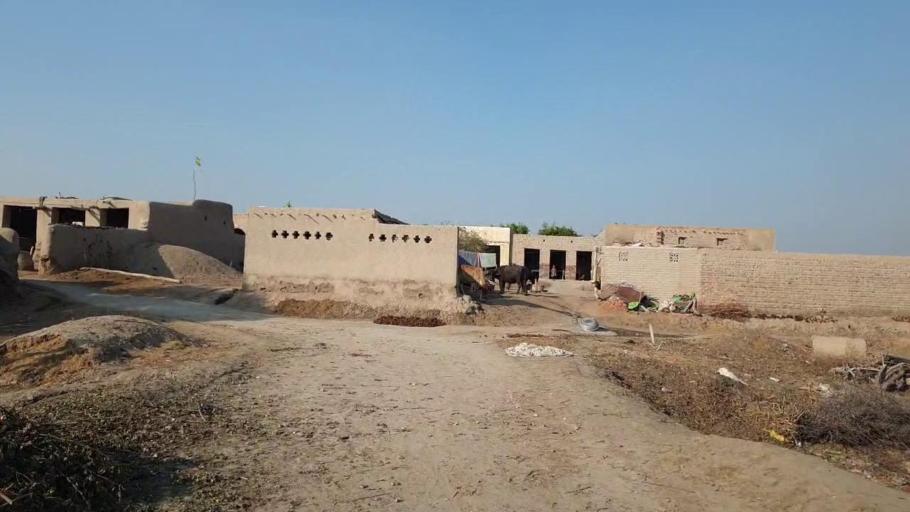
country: PK
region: Sindh
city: Sehwan
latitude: 26.4275
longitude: 67.7852
